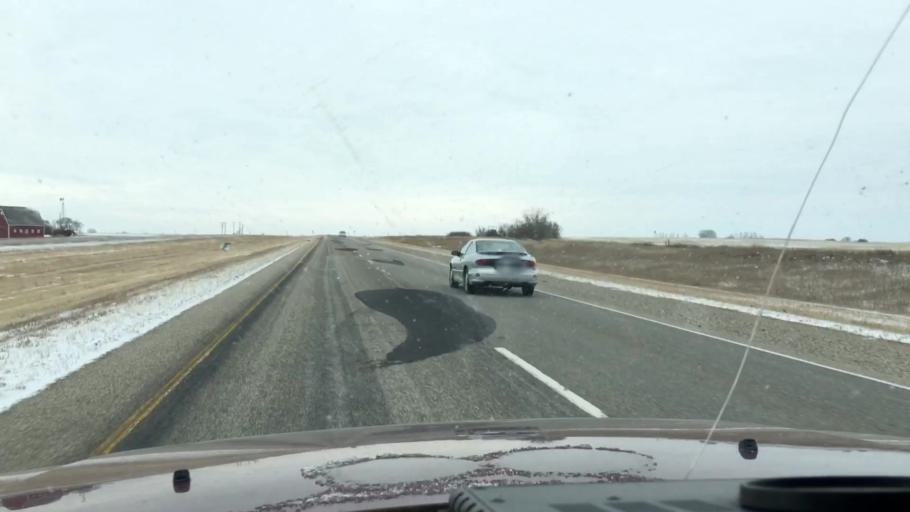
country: CA
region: Saskatchewan
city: Watrous
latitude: 51.4208
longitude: -106.1935
